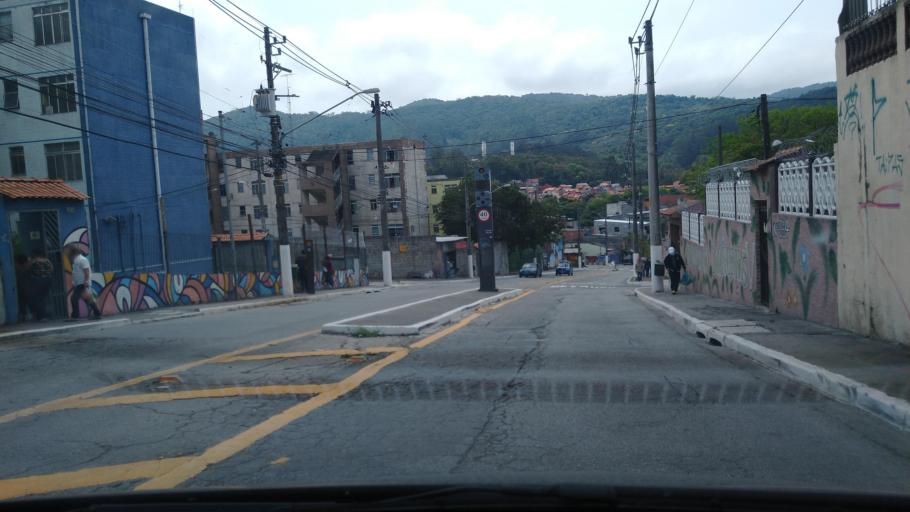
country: BR
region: Sao Paulo
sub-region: Caieiras
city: Caieiras
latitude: -23.4423
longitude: -46.7131
